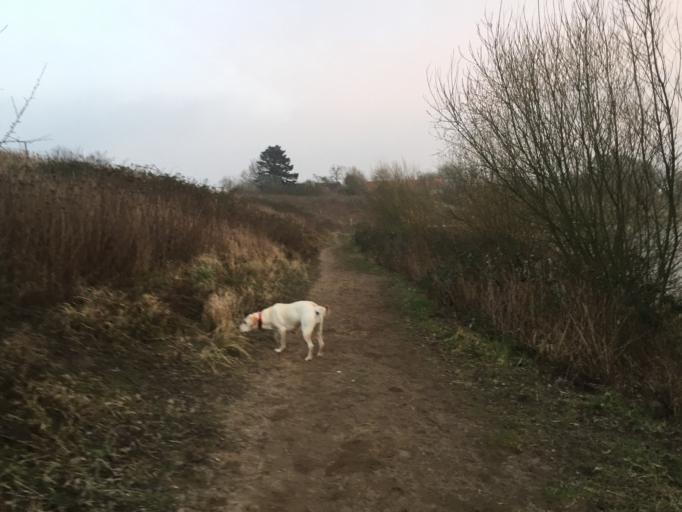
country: DK
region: South Denmark
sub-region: Kerteminde Kommune
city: Langeskov
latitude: 55.3315
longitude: 10.5298
